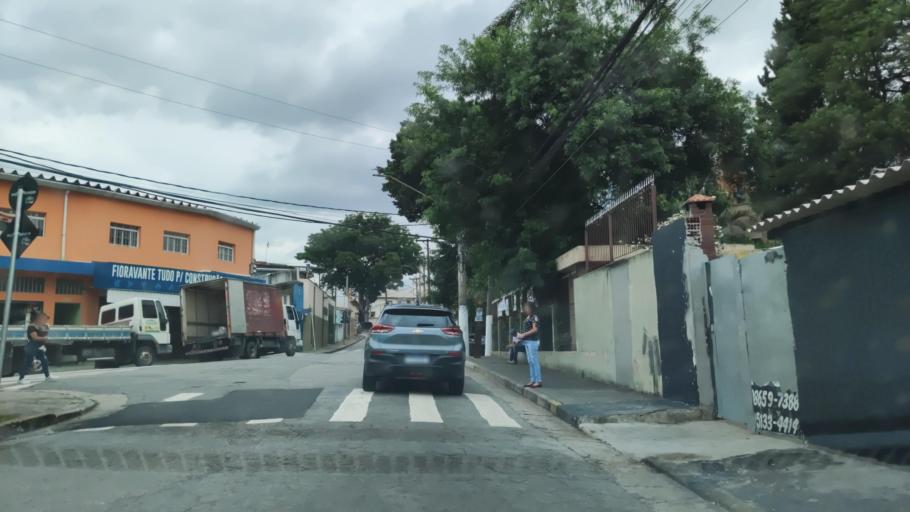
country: BR
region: Sao Paulo
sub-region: Sao Paulo
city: Sao Paulo
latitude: -23.4677
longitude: -46.6601
